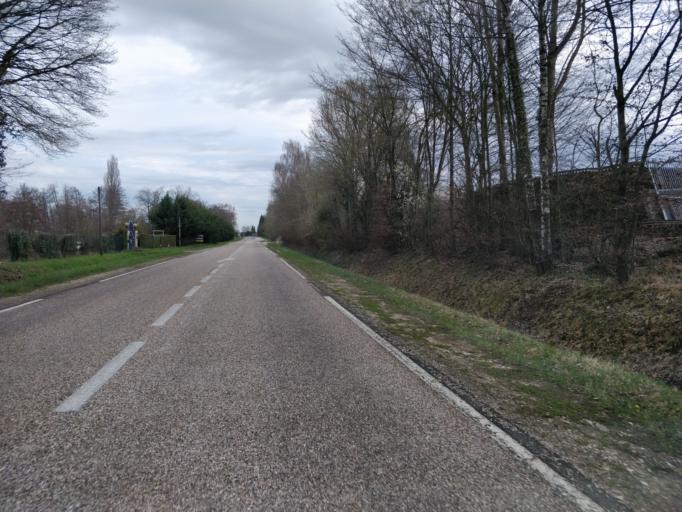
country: FR
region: Lorraine
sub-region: Departement de la Moselle
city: Uckange
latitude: 49.2912
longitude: 6.1347
